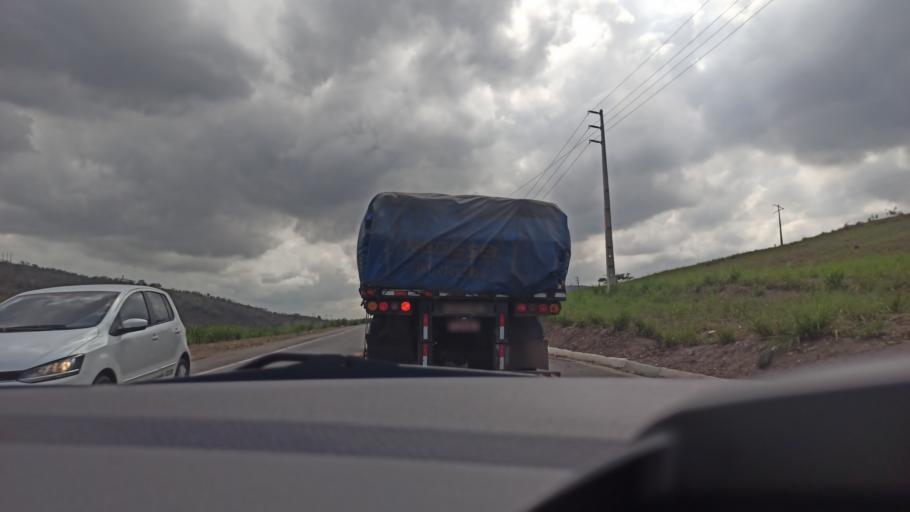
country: BR
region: Pernambuco
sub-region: Timbauba
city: Timbauba
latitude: -7.5226
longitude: -35.2956
